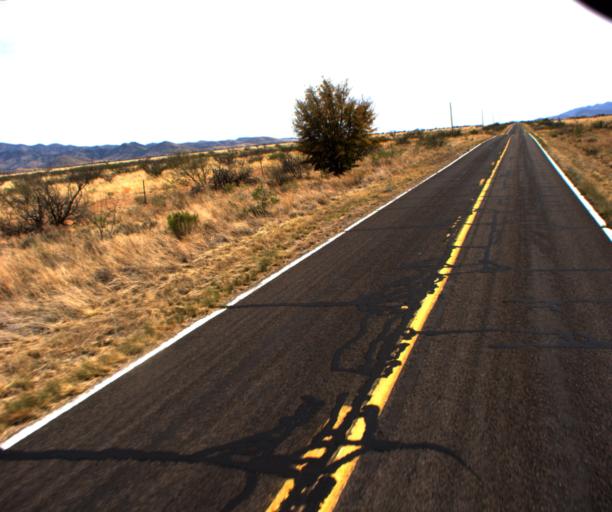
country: US
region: Arizona
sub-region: Cochise County
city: Willcox
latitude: 31.9127
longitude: -109.4915
